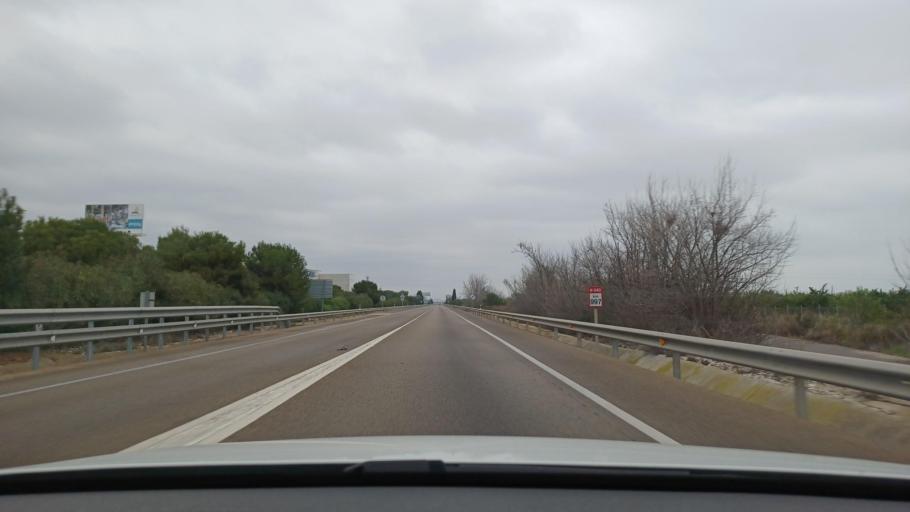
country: ES
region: Valencia
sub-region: Provincia de Castello
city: Orpesa/Oropesa del Mar
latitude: 40.1057
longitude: 0.1368
